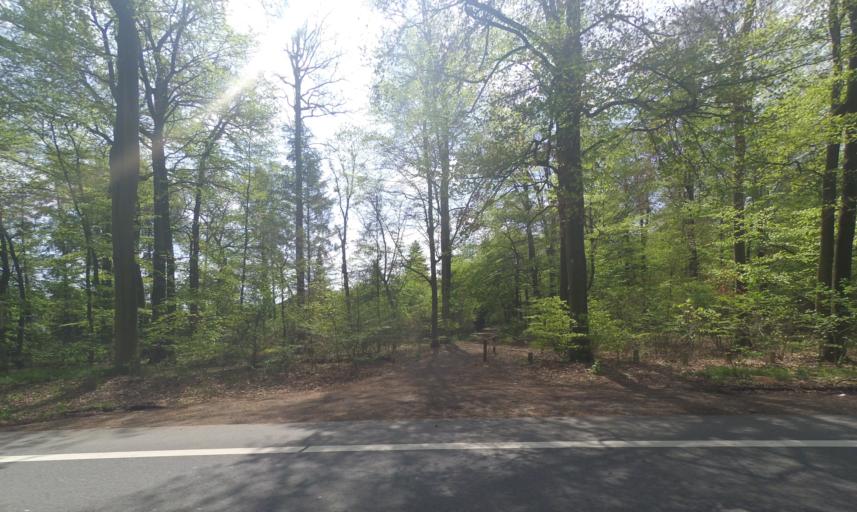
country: DE
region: Hesse
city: Heusenstamm
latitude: 50.0591
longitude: 8.7817
